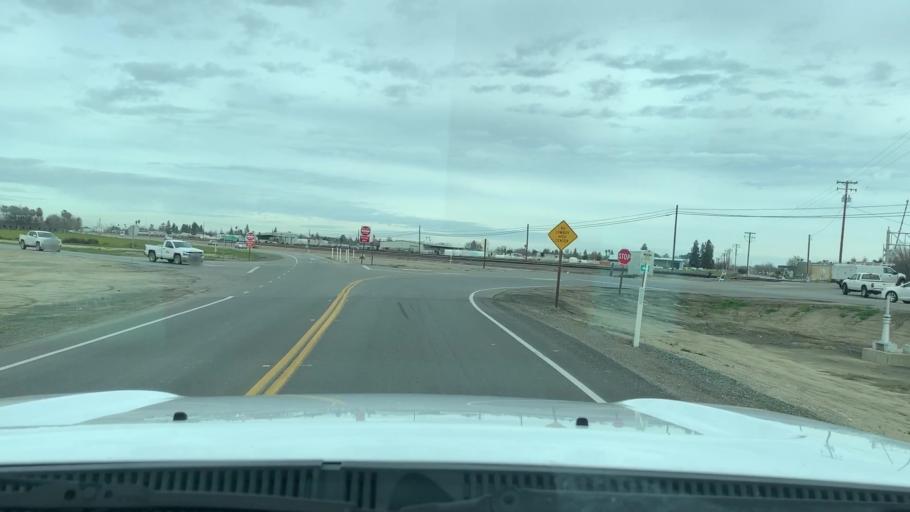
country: US
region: California
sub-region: Kern County
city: Shafter
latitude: 35.4917
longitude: -119.2609
